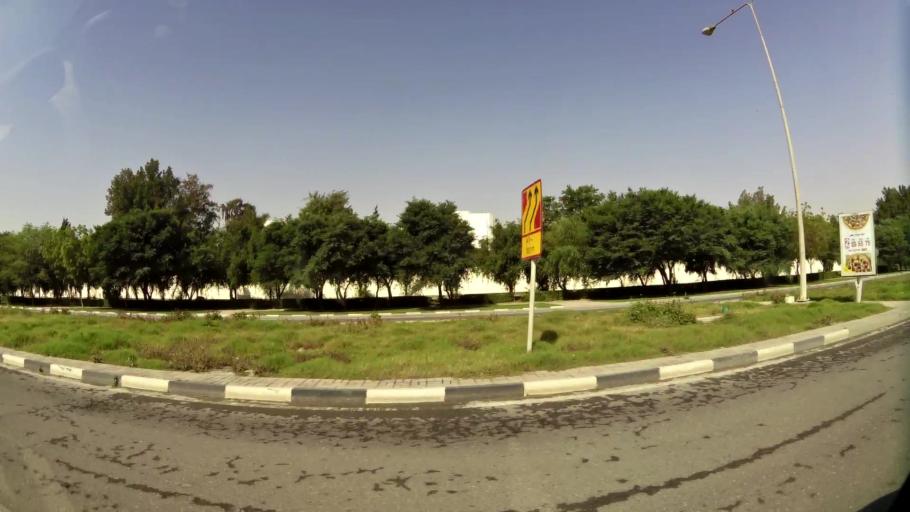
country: QA
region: Baladiyat ad Dawhah
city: Doha
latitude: 25.3268
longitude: 51.5170
